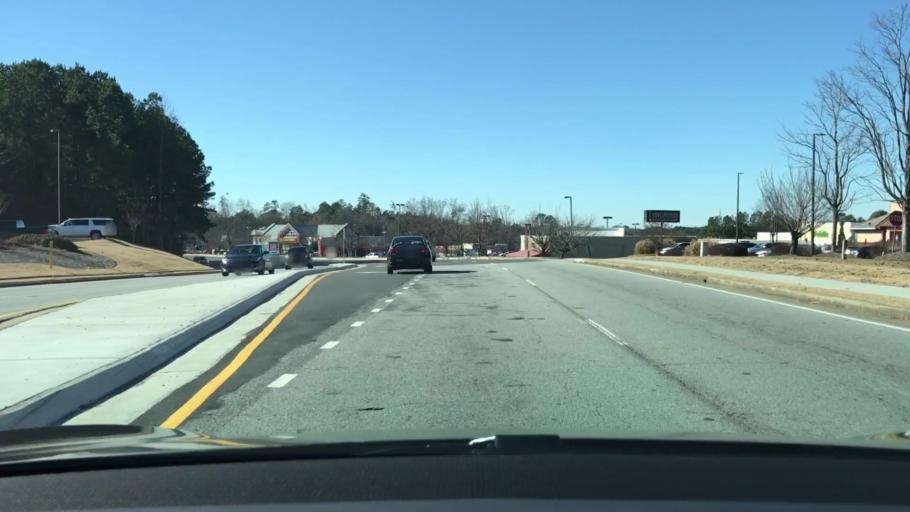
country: US
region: Georgia
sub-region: Gwinnett County
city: Lawrenceville
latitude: 33.9695
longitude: -84.0210
